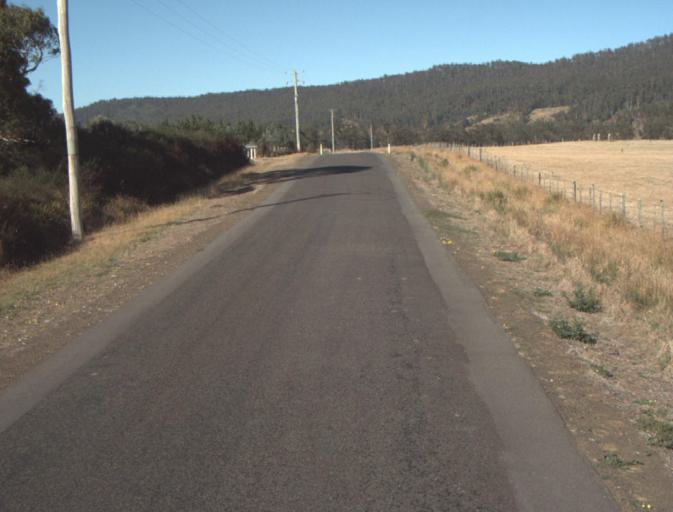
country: AU
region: Tasmania
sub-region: Launceston
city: Newstead
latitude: -41.3284
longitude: 147.3114
